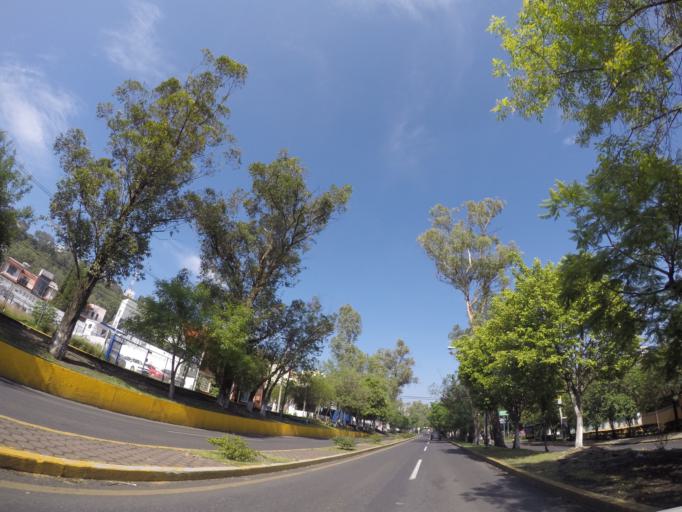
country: MX
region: Michoacan
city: Morelia
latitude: 19.6813
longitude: -101.1832
